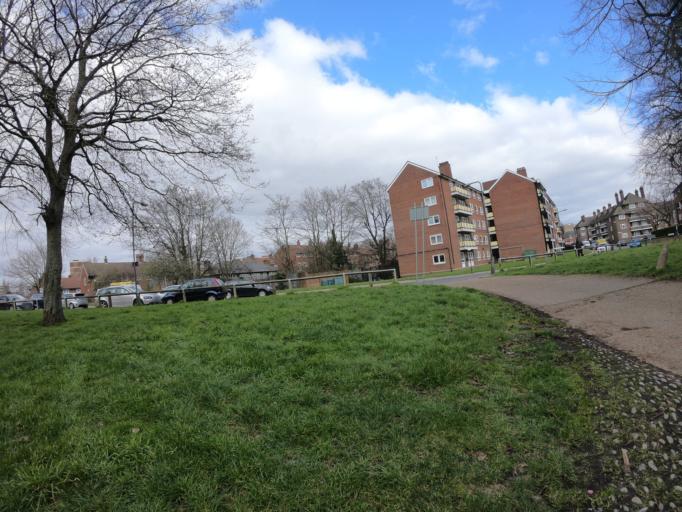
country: GB
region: England
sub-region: Greater London
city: Woolwich
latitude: 51.4908
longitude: 0.0577
